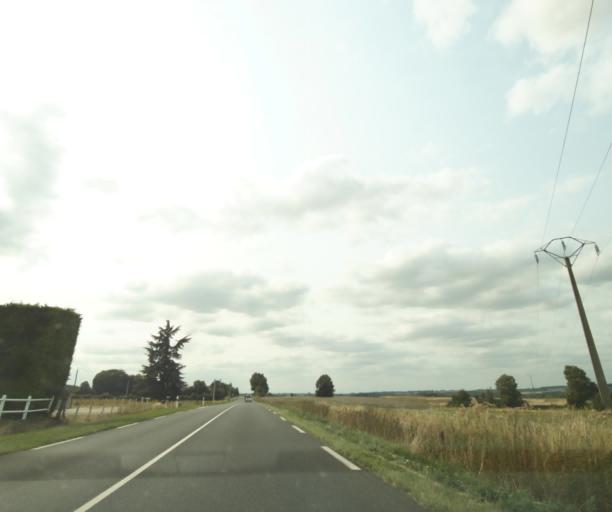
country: FR
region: Centre
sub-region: Departement de l'Indre
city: Clion
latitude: 46.9217
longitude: 1.2993
